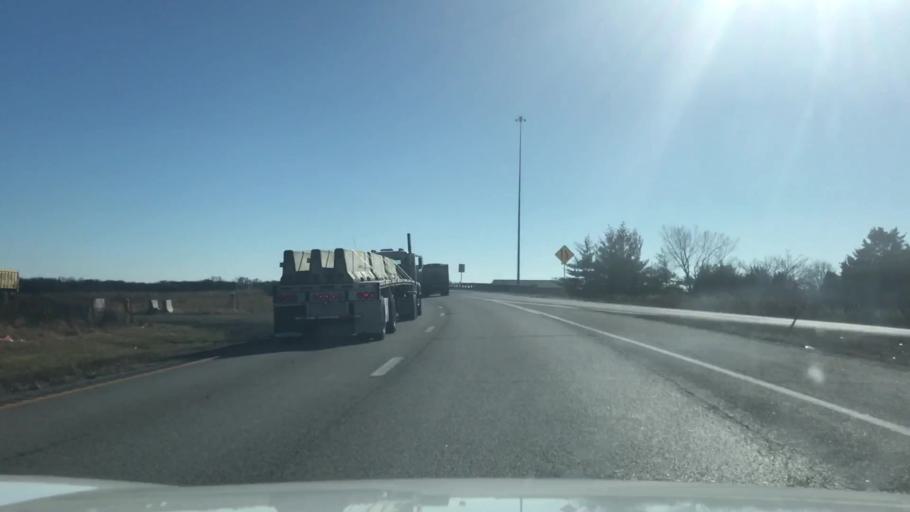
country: US
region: Missouri
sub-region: Saint Charles County
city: Wentzville
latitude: 38.8077
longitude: -90.8401
